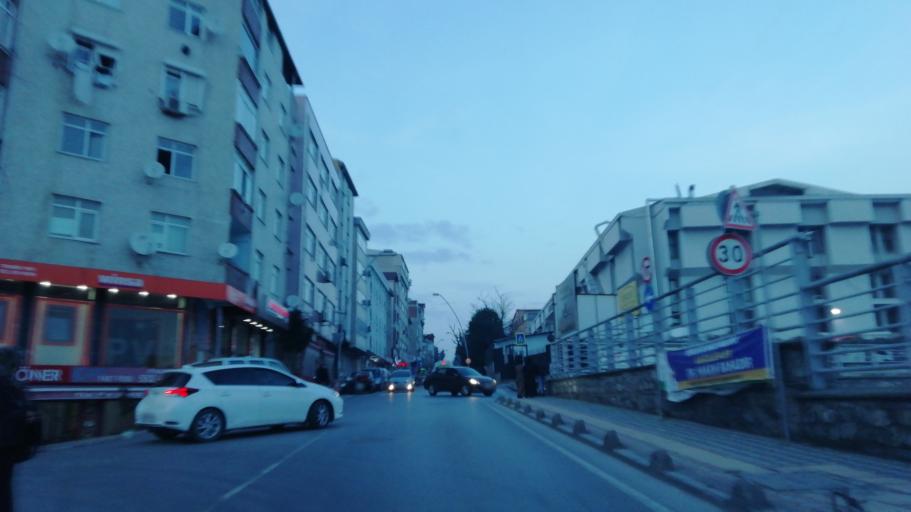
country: TR
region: Istanbul
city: Bahcelievler
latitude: 41.0068
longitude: 28.8219
